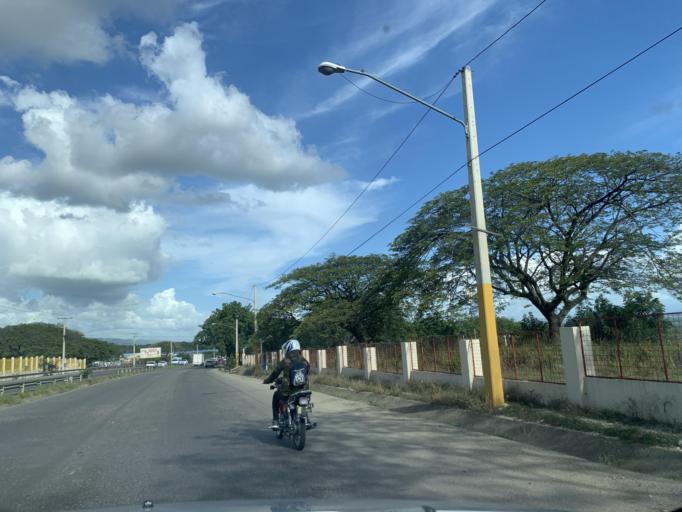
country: DO
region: Santiago
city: Villa Gonzalez
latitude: 19.5516
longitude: -70.8163
